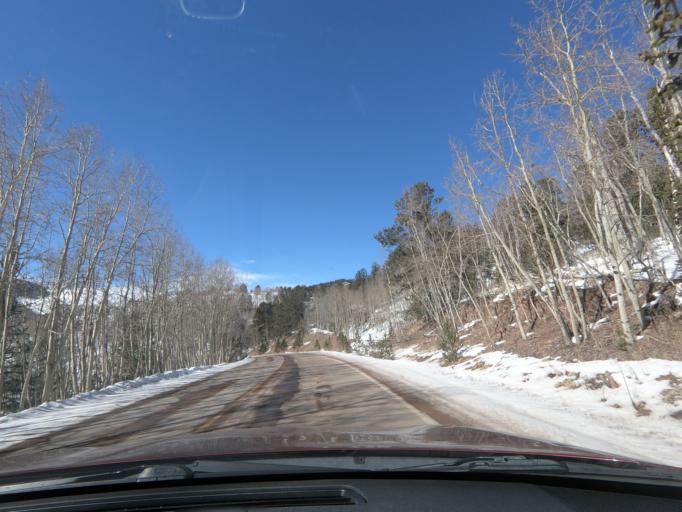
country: US
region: Colorado
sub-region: Teller County
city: Cripple Creek
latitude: 38.7433
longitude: -105.1051
